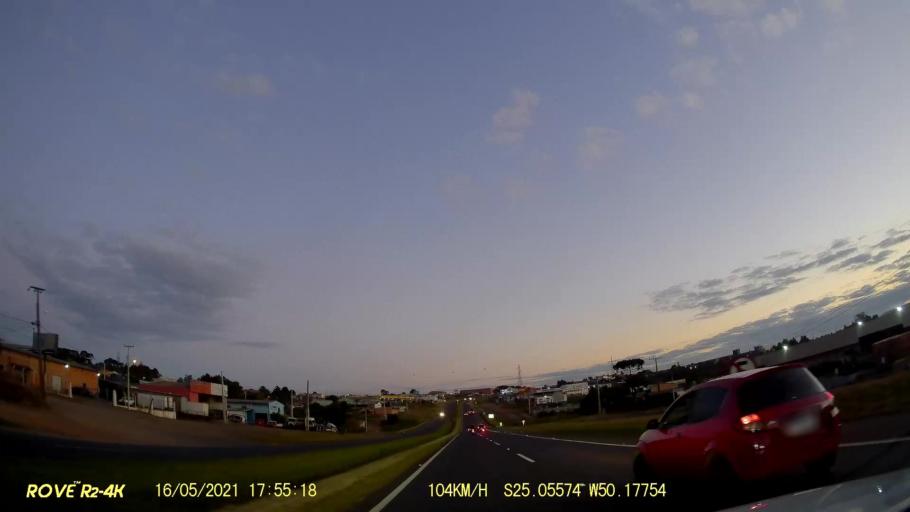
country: BR
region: Parana
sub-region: Ponta Grossa
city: Ponta Grossa
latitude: -25.0558
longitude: -50.1776
